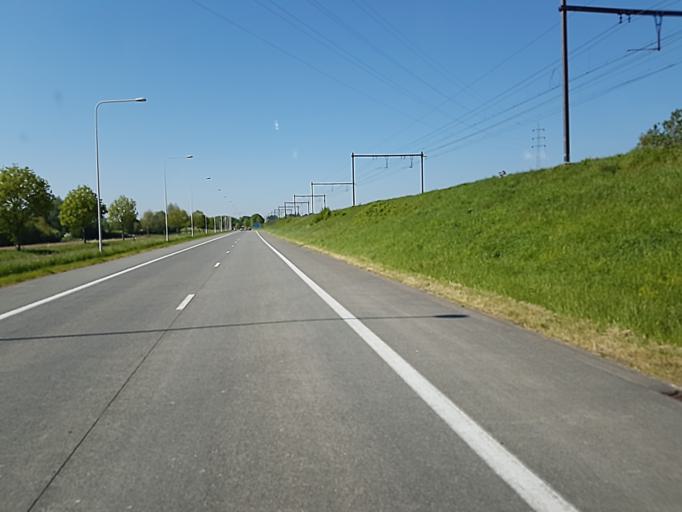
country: BE
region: Wallonia
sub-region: Province du Hainaut
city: Ath
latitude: 50.6454
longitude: 3.7802
